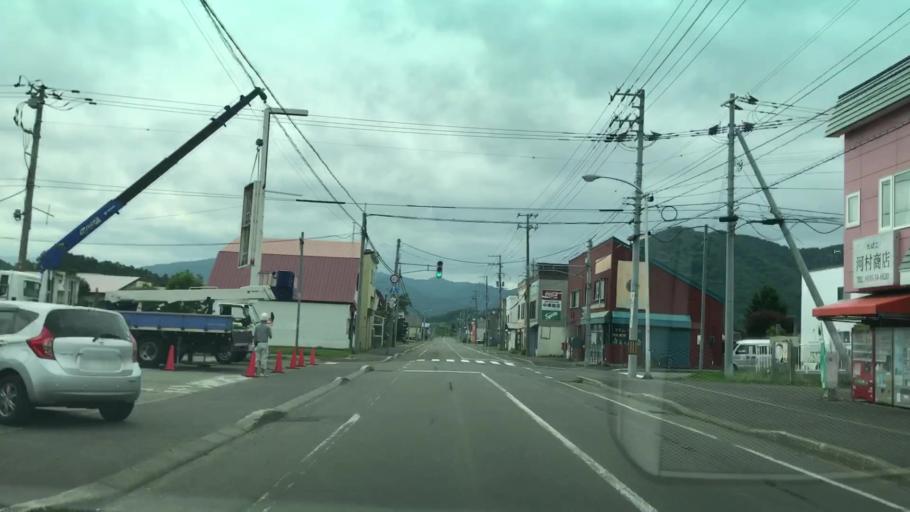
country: JP
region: Hokkaido
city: Yoichi
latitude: 43.0845
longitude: 140.8159
